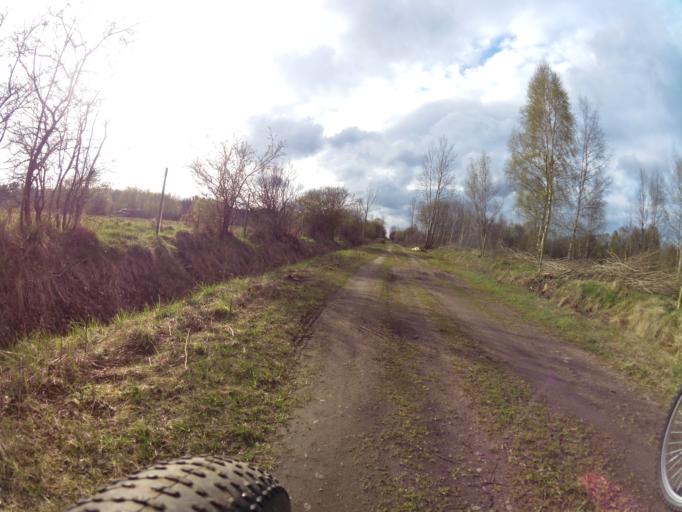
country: PL
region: West Pomeranian Voivodeship
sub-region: Powiat slawienski
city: Slawno
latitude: 54.3331
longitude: 16.7223
